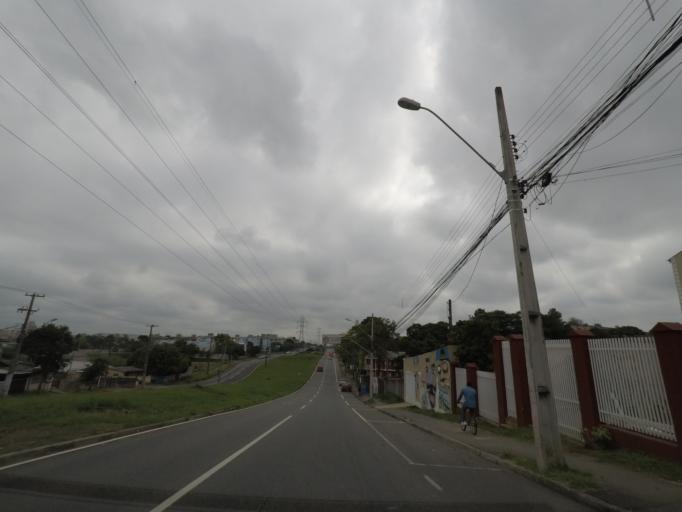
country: BR
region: Parana
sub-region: Curitiba
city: Curitiba
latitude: -25.4993
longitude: -49.3171
